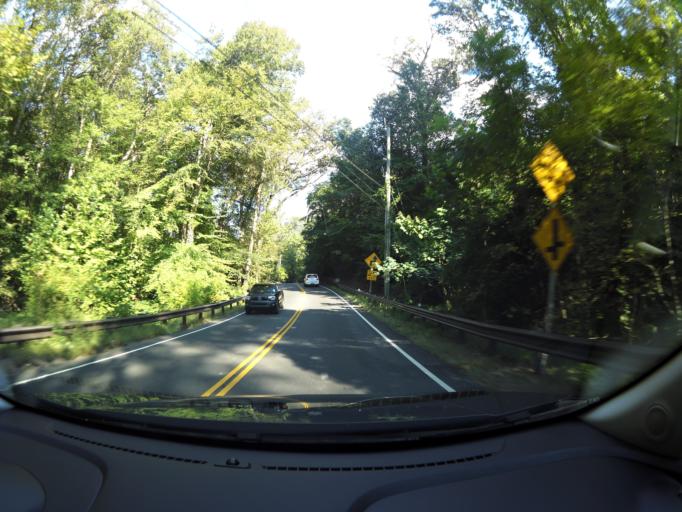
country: US
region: Virginia
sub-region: Fairfax County
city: McLean
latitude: 38.9591
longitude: -77.2076
